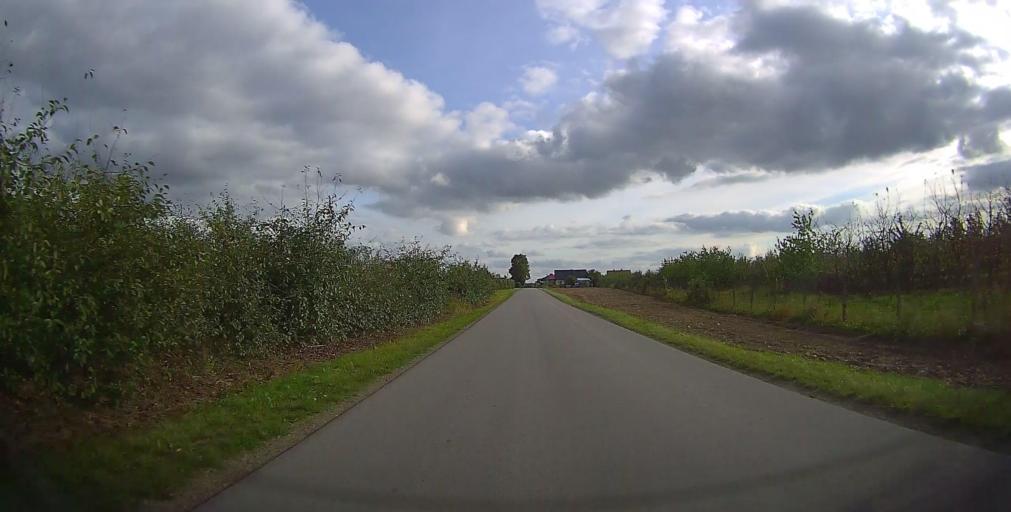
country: PL
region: Masovian Voivodeship
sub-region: Powiat bialobrzeski
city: Promna
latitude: 51.7430
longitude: 20.9653
